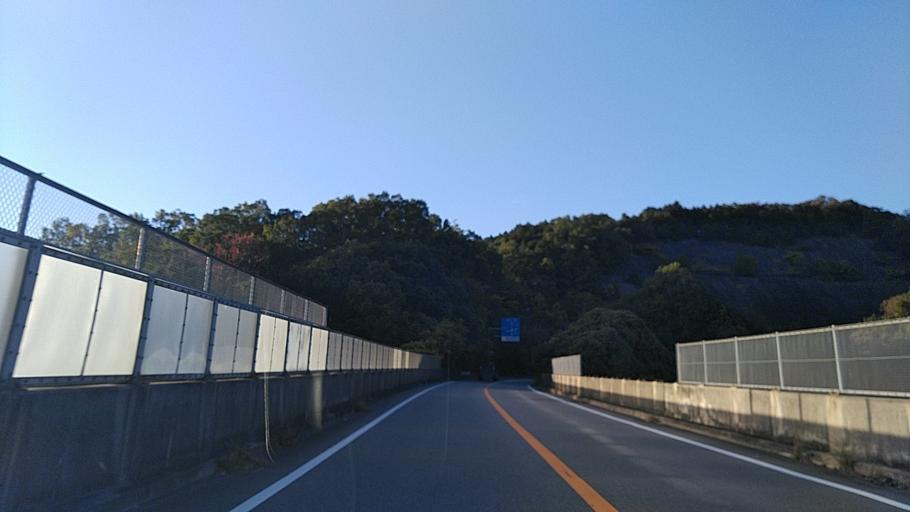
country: JP
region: Osaka
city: Ikeda
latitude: 34.9034
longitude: 135.4082
